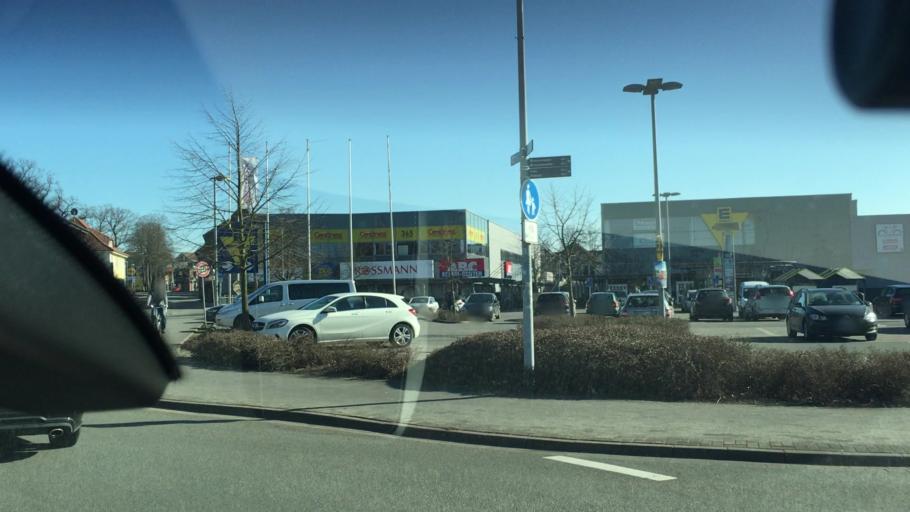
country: DE
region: Lower Saxony
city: Lohne
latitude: 52.6679
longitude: 8.2306
